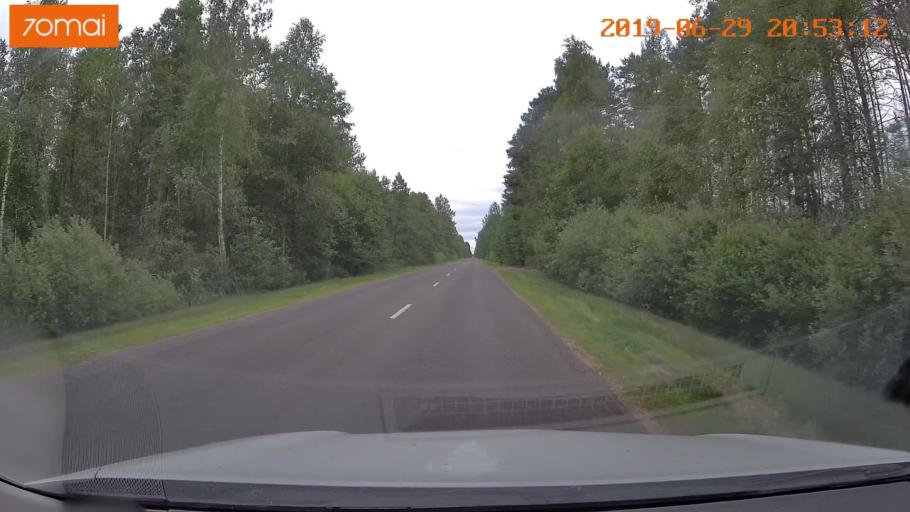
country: BY
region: Brest
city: Hantsavichy
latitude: 52.6988
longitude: 26.3621
